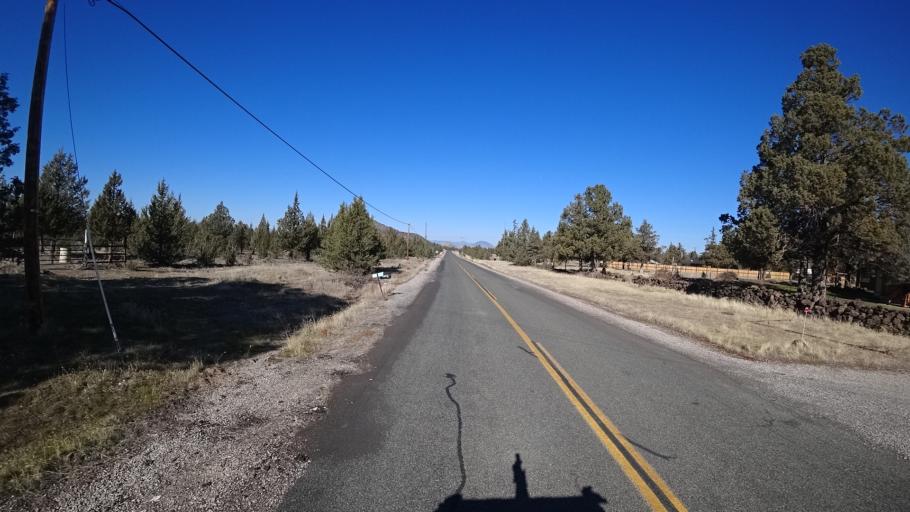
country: US
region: California
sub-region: Siskiyou County
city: Montague
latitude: 41.6522
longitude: -122.3605
